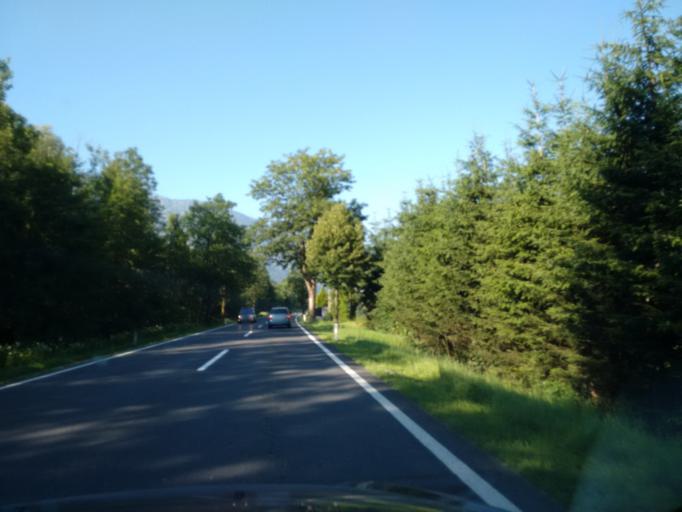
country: AT
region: Upper Austria
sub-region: Politischer Bezirk Gmunden
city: Ebensee
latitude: 47.7702
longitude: 13.7225
